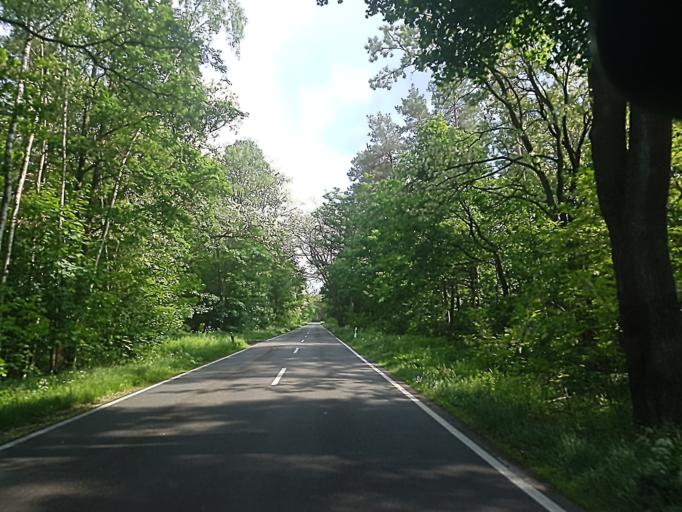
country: DE
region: Saxony-Anhalt
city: Klieken
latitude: 51.9551
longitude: 12.3495
